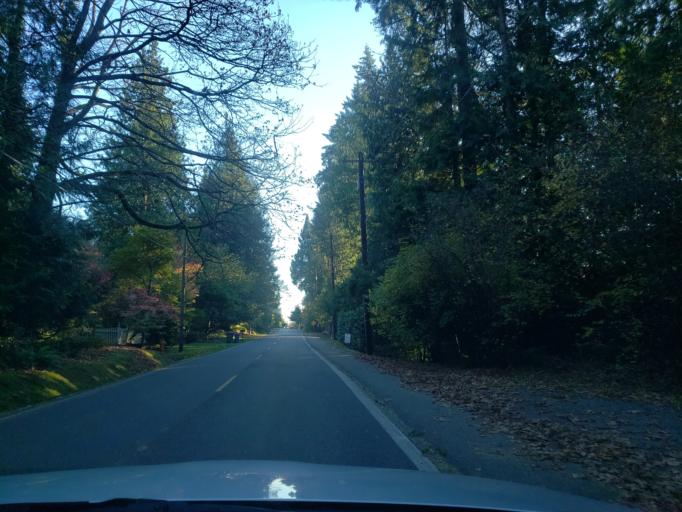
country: US
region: Washington
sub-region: Snohomish County
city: Woodway
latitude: 47.7855
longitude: -122.3856
